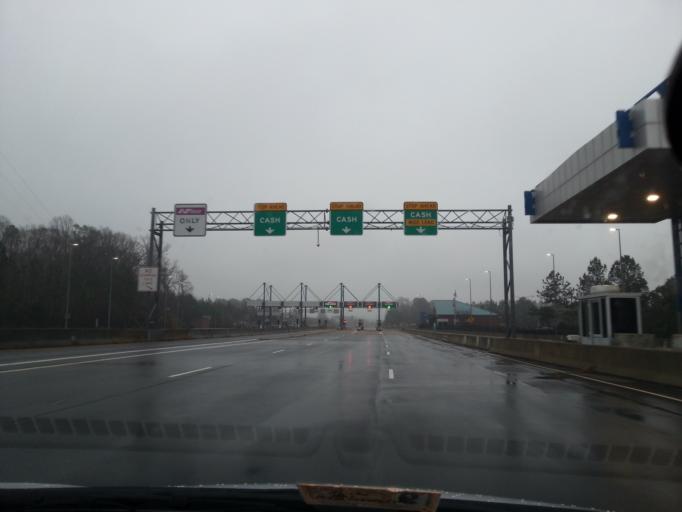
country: US
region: North Carolina
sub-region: Currituck County
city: Moyock
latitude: 36.6097
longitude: -76.2057
